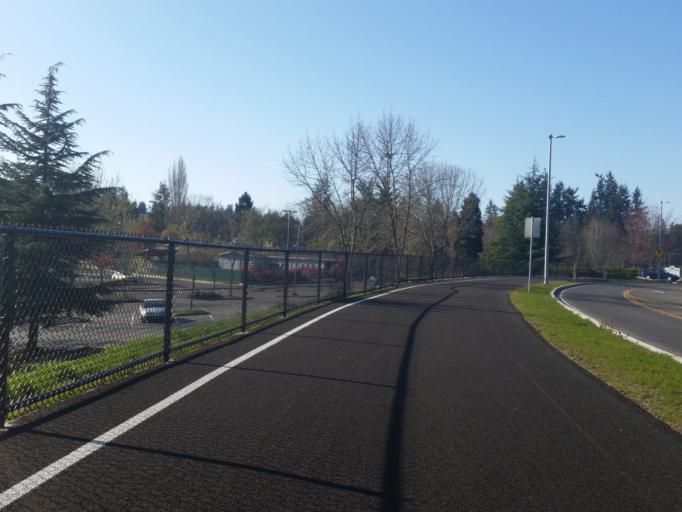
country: US
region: Washington
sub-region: Snohomish County
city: Mountlake Terrace
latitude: 47.7889
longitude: -122.3283
